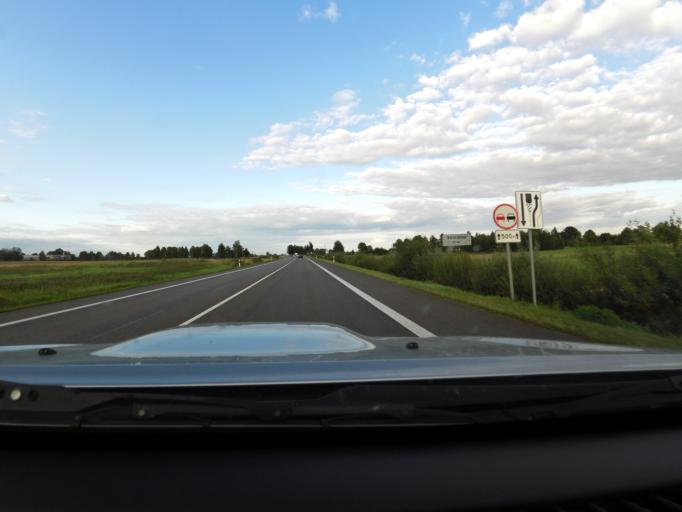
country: LT
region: Kauno apskritis
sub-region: Kauno rajonas
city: Mastaiciai
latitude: 54.7596
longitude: 23.7452
